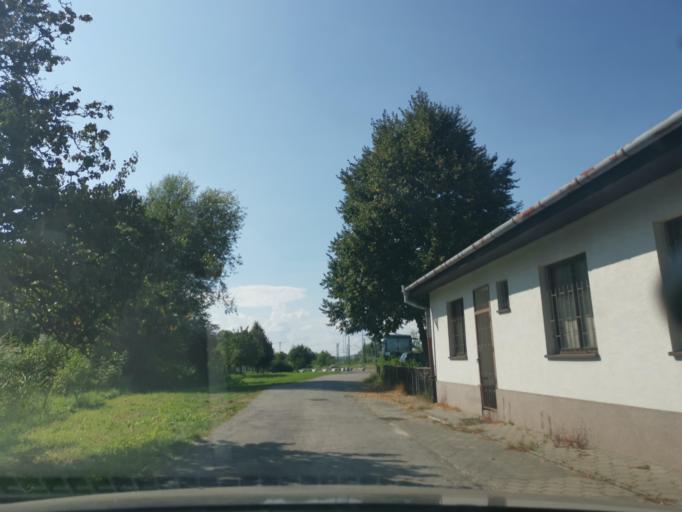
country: SK
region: Trnavsky
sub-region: Okres Senica
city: Senica
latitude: 48.6597
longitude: 17.2628
